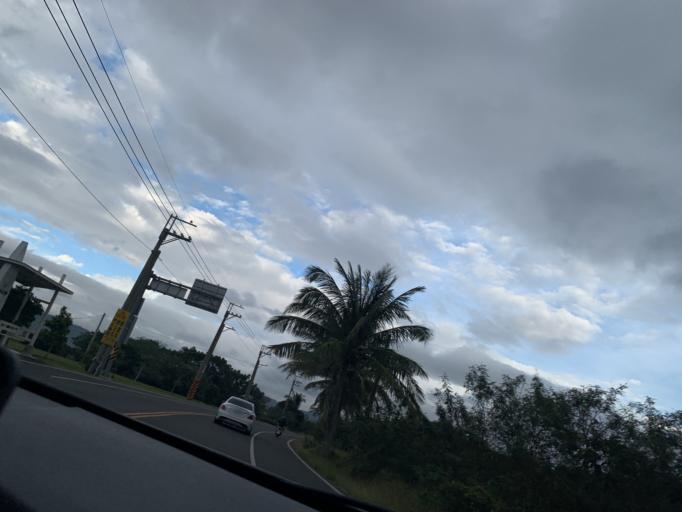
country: TW
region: Taiwan
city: Hengchun
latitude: 22.0482
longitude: 120.7037
